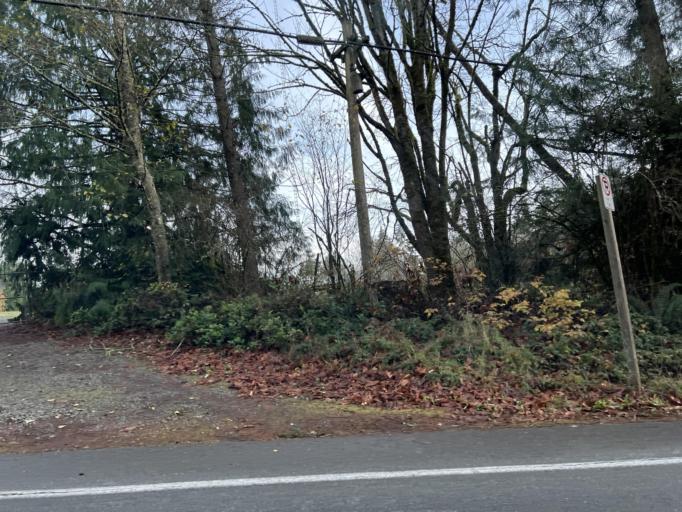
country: US
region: Washington
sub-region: Kitsap County
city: Bainbridge Island
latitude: 47.6547
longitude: -122.5189
